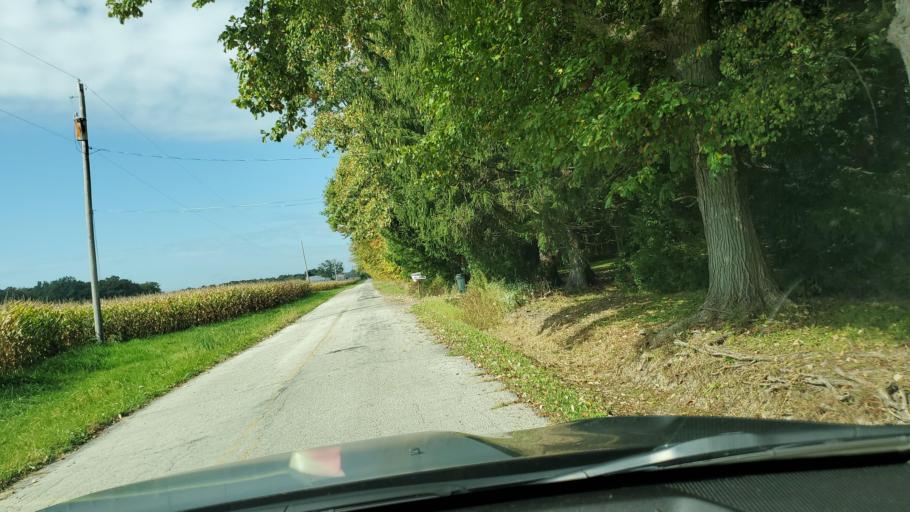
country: US
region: Ohio
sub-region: Trumbull County
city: Cortland
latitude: 41.4126
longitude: -80.6376
